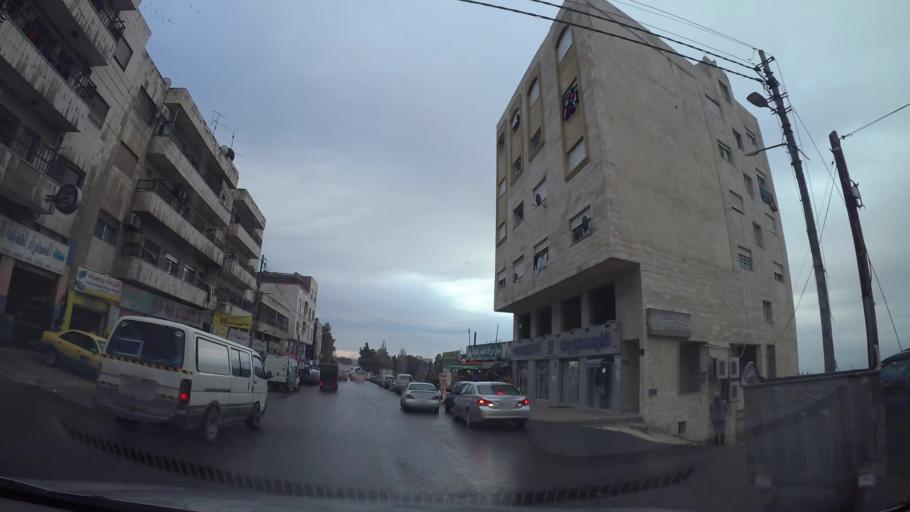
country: JO
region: Amman
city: Al Jubayhah
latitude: 32.0290
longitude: 35.8342
